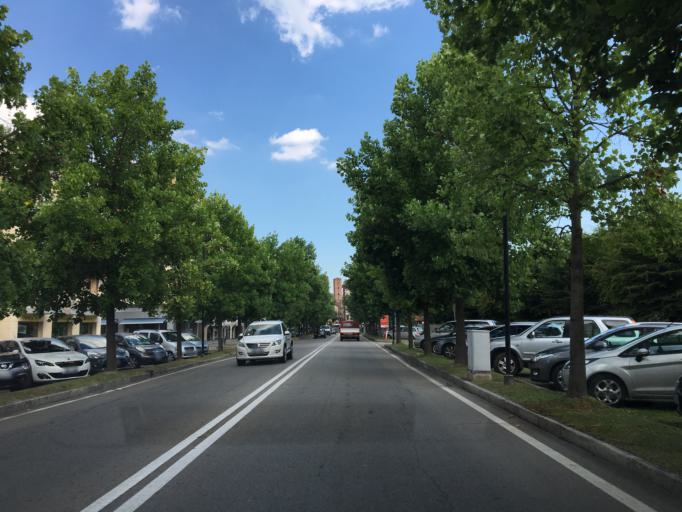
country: IT
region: Piedmont
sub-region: Provincia di Cuneo
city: Alba
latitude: 44.7035
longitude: 8.0300
